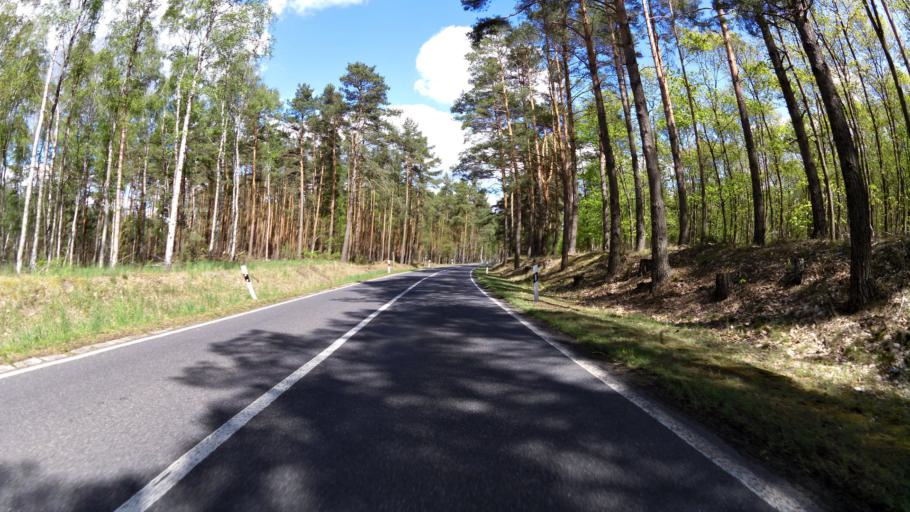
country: DE
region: Brandenburg
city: Wendisch Rietz
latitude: 52.1441
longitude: 13.9682
